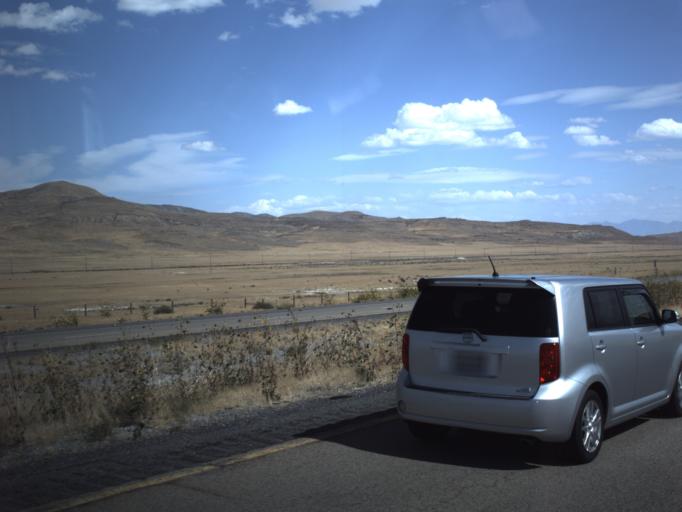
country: US
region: Utah
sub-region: Tooele County
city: Grantsville
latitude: 40.8101
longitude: -112.8682
